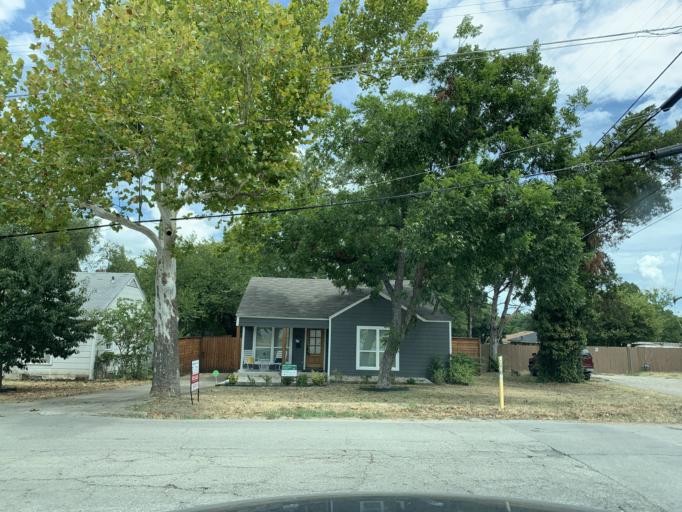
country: US
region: Texas
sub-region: Dallas County
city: Cockrell Hill
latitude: 32.7374
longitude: -96.8797
